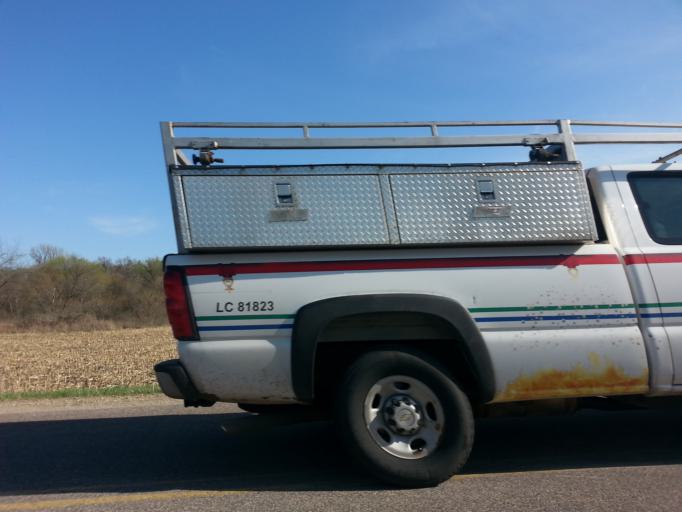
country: US
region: Wisconsin
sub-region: Pierce County
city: Ellsworth
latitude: 44.7355
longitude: -92.5799
